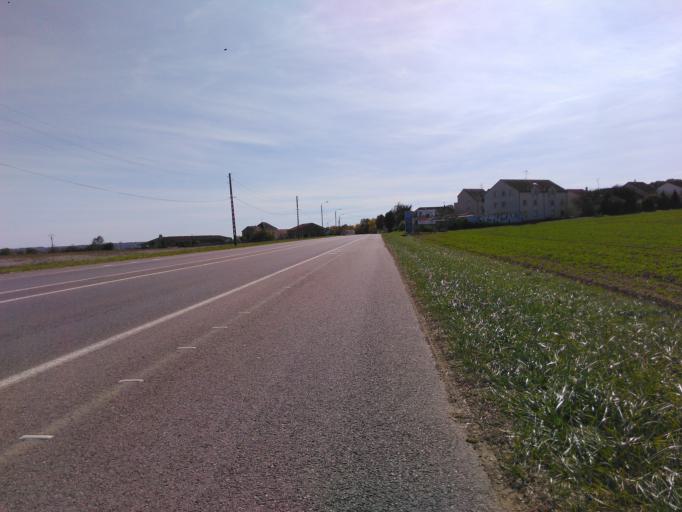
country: FR
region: Lorraine
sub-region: Departement de la Moselle
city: Thionville
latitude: 49.3874
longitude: 6.1685
